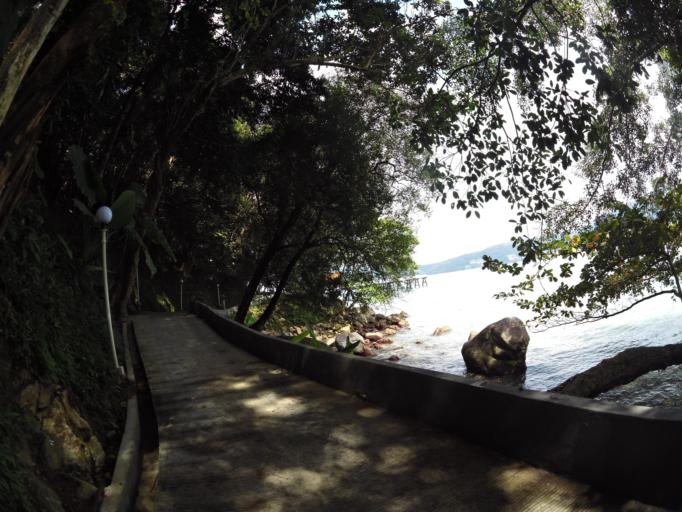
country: TH
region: Phuket
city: Patong
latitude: 7.8877
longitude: 98.2815
